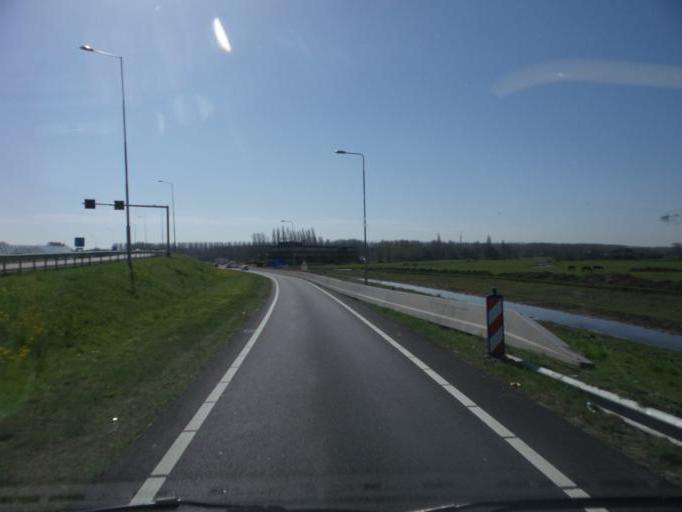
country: NL
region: South Holland
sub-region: Bodegraven-Reeuwijk
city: Bodegraven
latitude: 52.0722
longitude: 4.7393
